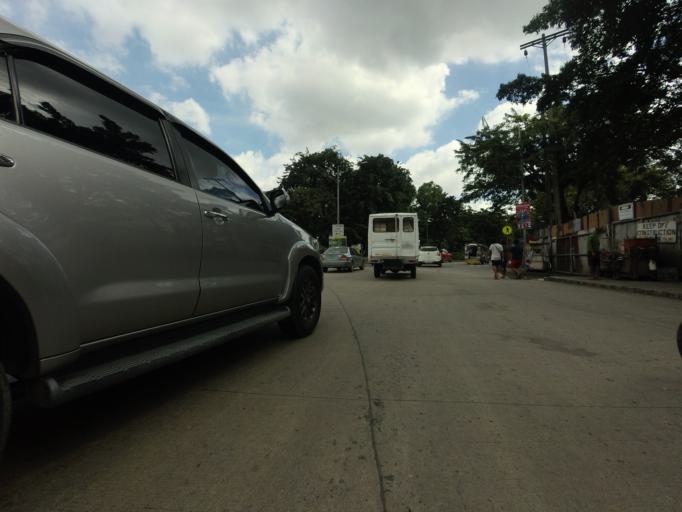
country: PH
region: Metro Manila
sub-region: City of Manila
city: Port Area
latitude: 14.5904
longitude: 120.9708
